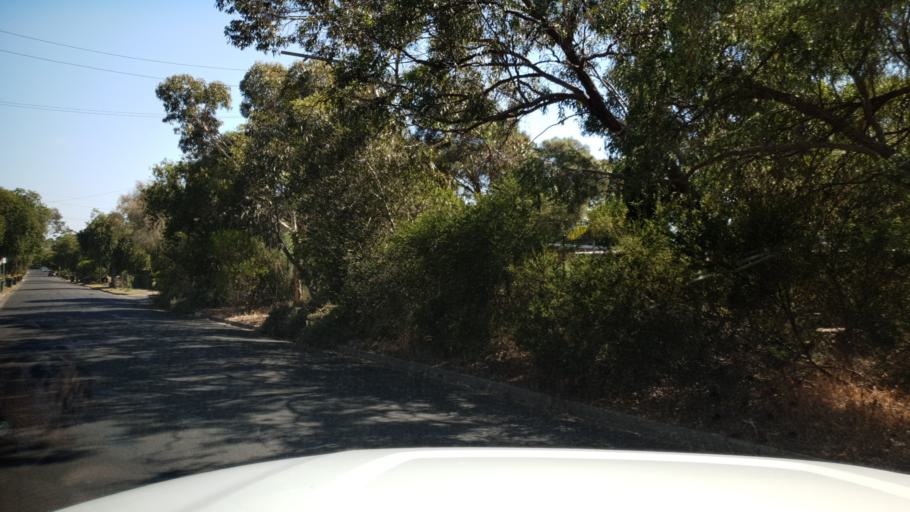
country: AU
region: South Australia
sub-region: Mitcham
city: Clapham
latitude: -34.9960
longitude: 138.5868
